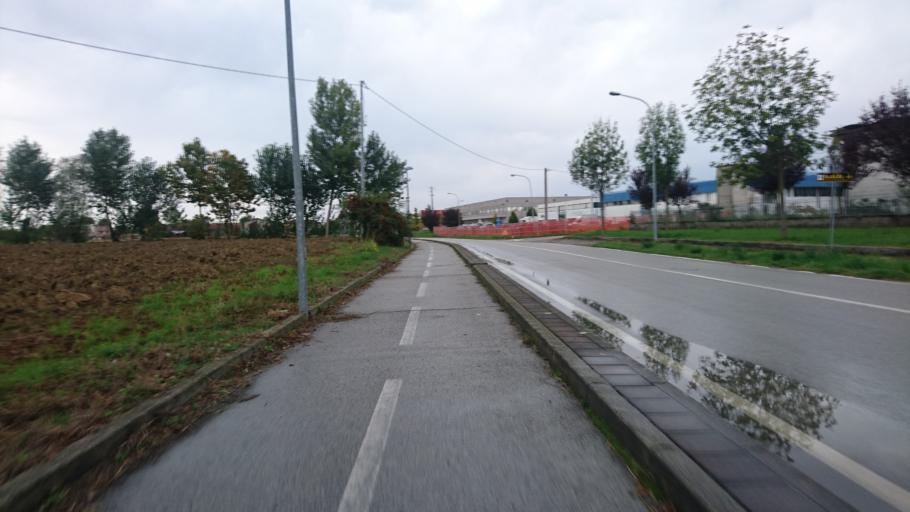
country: IT
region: Veneto
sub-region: Provincia di Padova
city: Veggiano
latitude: 45.4571
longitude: 11.6957
